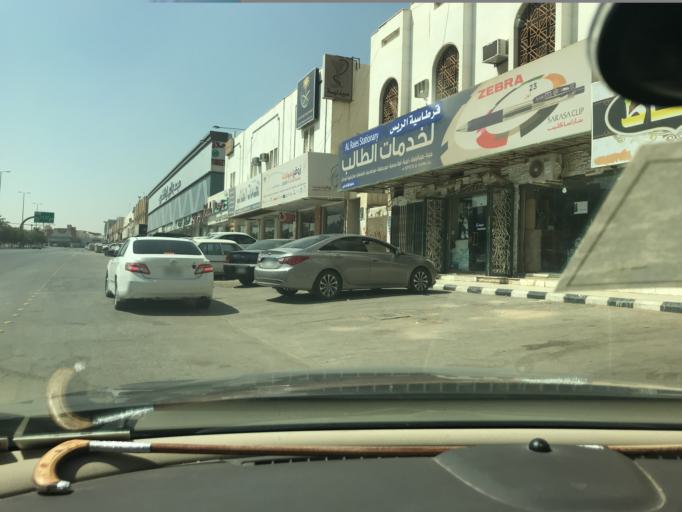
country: SA
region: Ar Riyad
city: Riyadh
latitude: 24.7043
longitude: 46.7813
